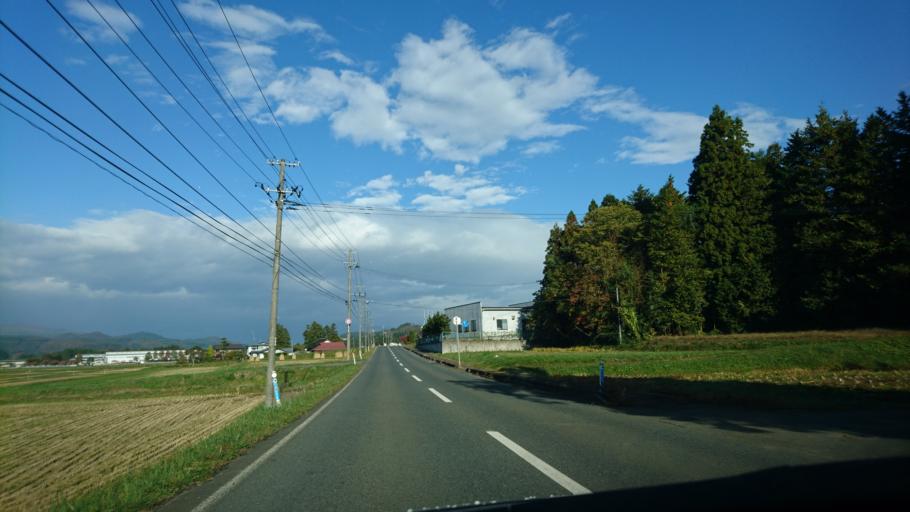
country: JP
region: Iwate
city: Mizusawa
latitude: 39.0251
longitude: 141.0856
